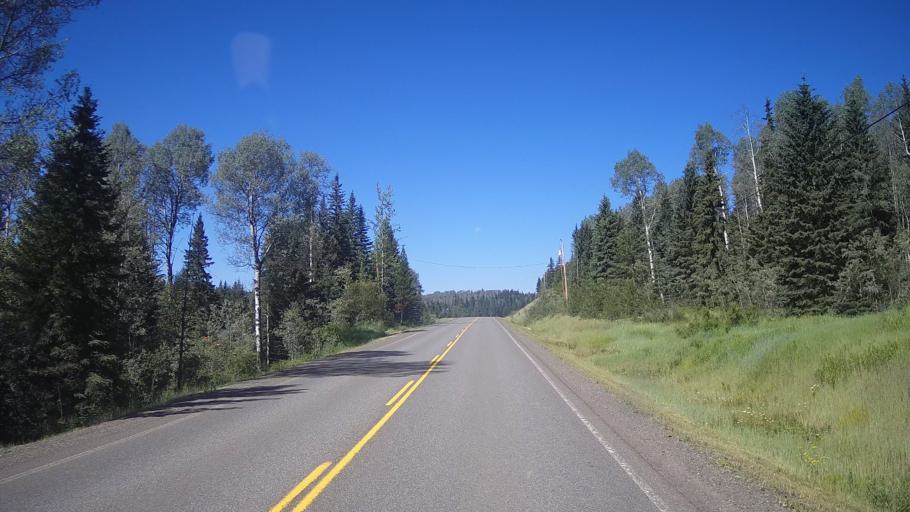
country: CA
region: British Columbia
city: Kamloops
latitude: 51.5037
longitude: -120.6191
